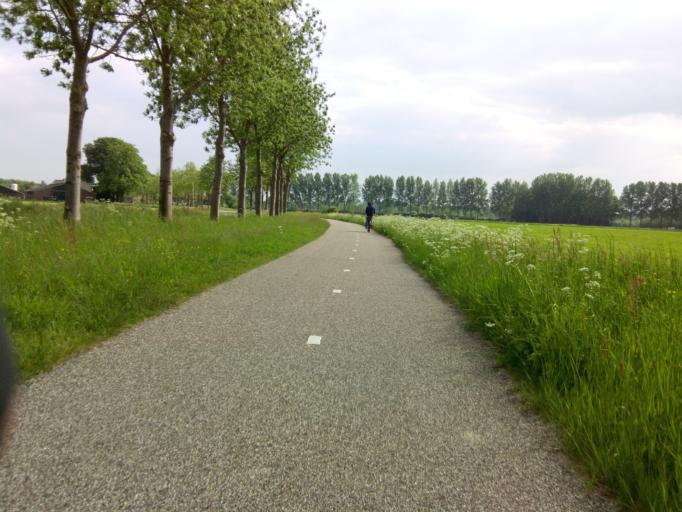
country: NL
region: Gelderland
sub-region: Berkelland
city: Borculo
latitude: 52.1045
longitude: 6.5253
